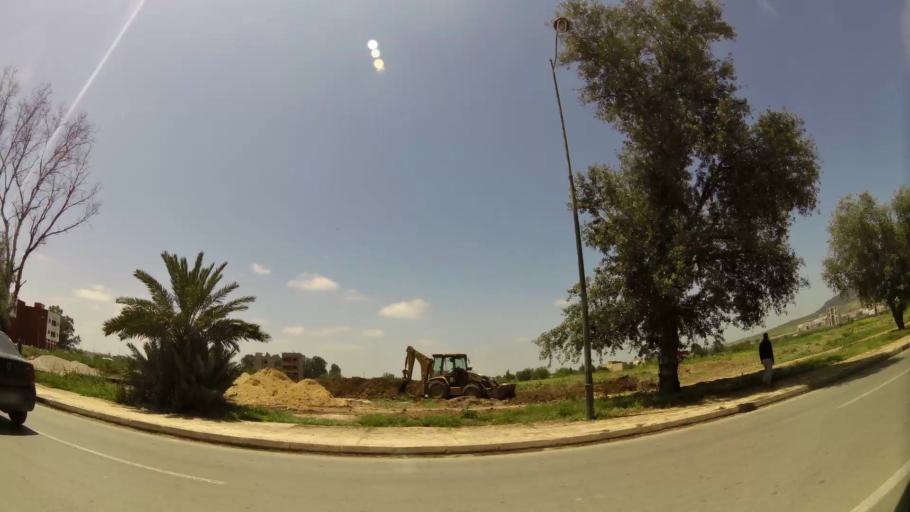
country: MA
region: Fes-Boulemane
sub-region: Fes
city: Fes
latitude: 34.0424
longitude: -5.0355
